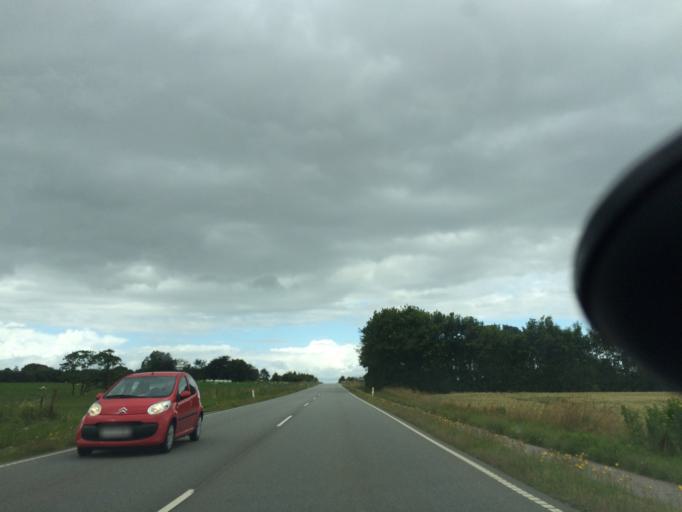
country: DK
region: Central Jutland
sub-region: Skanderborg Kommune
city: Galten
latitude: 56.1485
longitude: 9.8493
